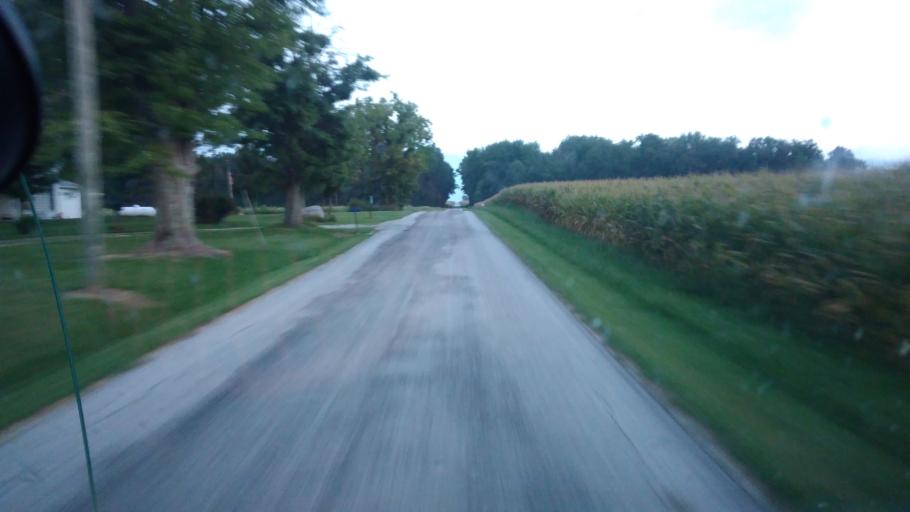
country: US
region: Ohio
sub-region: Hardin County
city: Kenton
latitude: 40.6557
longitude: -83.4588
